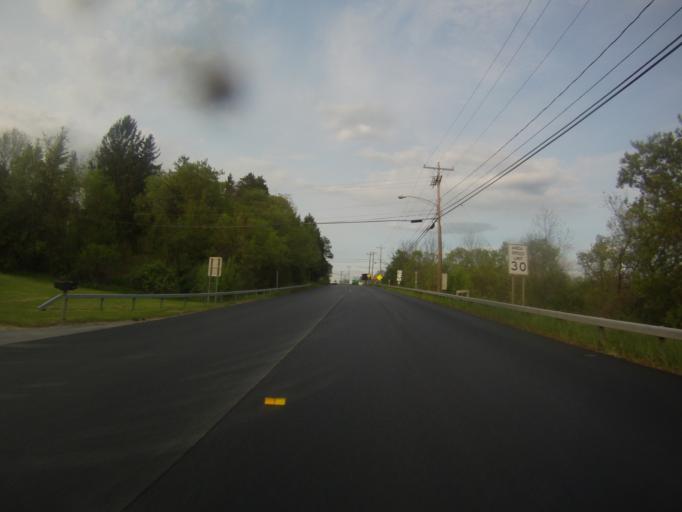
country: US
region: New York
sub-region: Essex County
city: Ticonderoga
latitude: 43.8469
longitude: -73.4378
